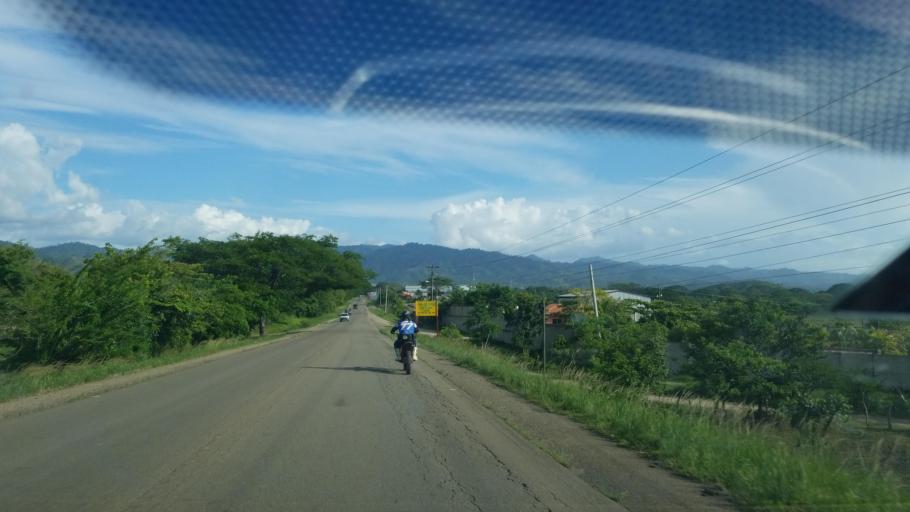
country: HN
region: El Paraiso
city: Cuyali
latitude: 13.9036
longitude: -86.5559
